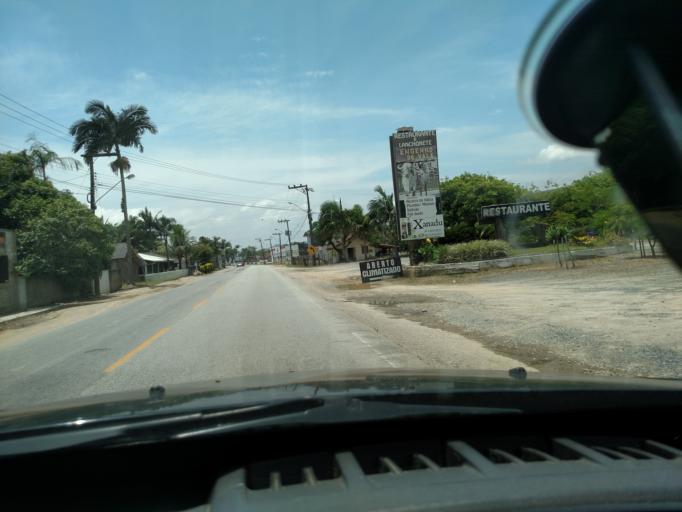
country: BR
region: Santa Catarina
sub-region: Gaspar
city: Gaspar
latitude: -26.9104
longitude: -48.8561
